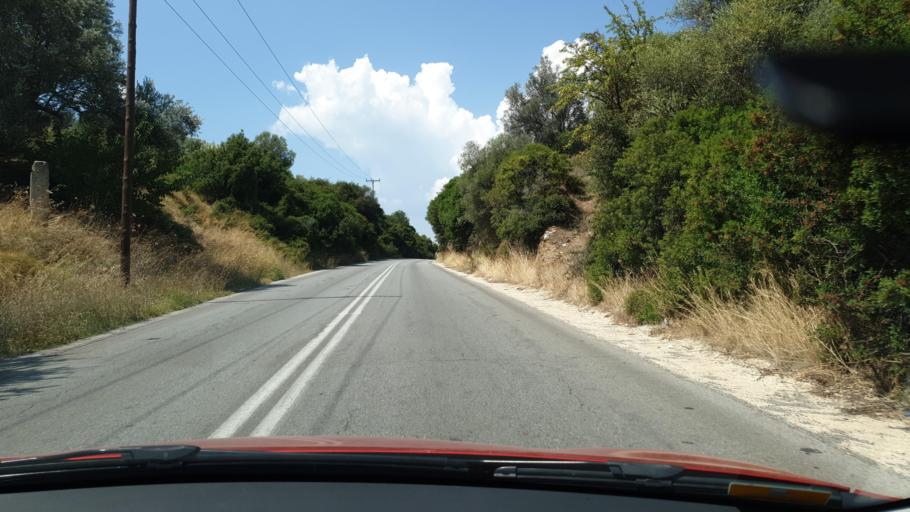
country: GR
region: Central Greece
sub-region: Nomos Evvoias
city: Aliveri
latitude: 38.3919
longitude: 24.0873
